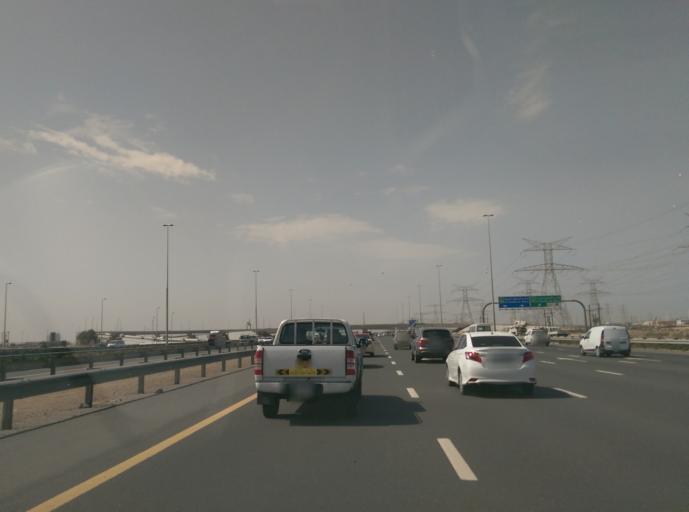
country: AE
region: Dubai
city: Dubai
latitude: 25.1237
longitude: 55.2521
